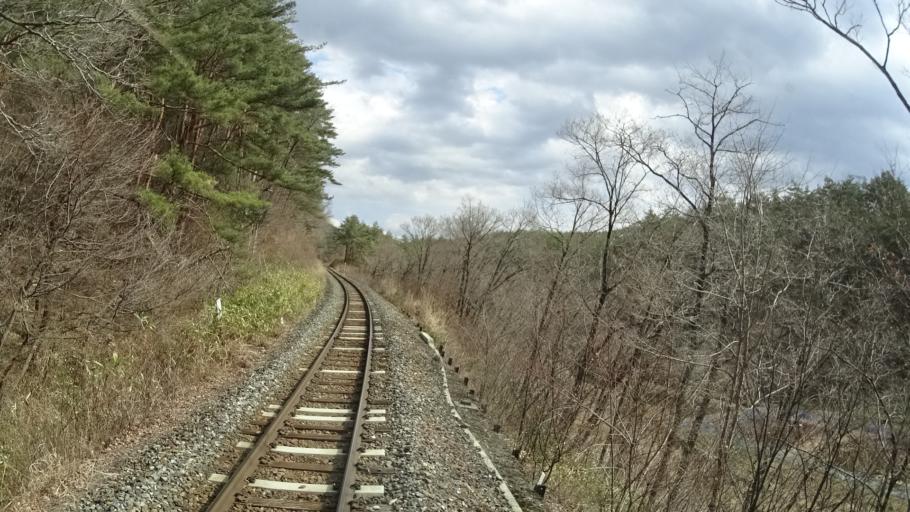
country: JP
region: Iwate
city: Tono
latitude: 39.3369
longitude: 141.3537
